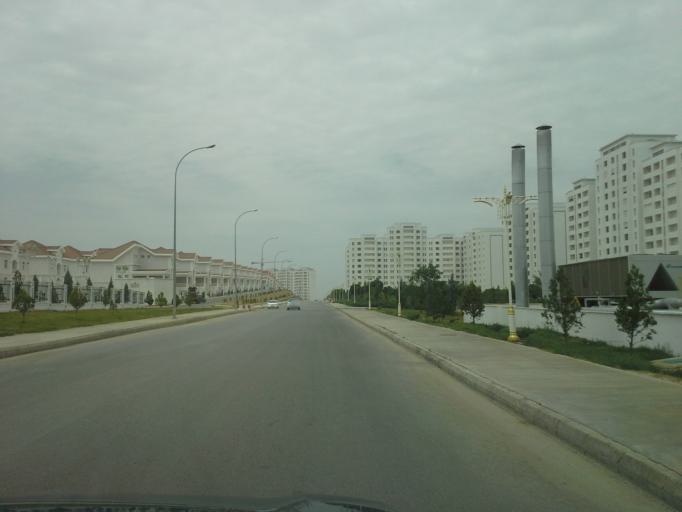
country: TM
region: Ahal
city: Ashgabat
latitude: 37.9303
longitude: 58.3664
